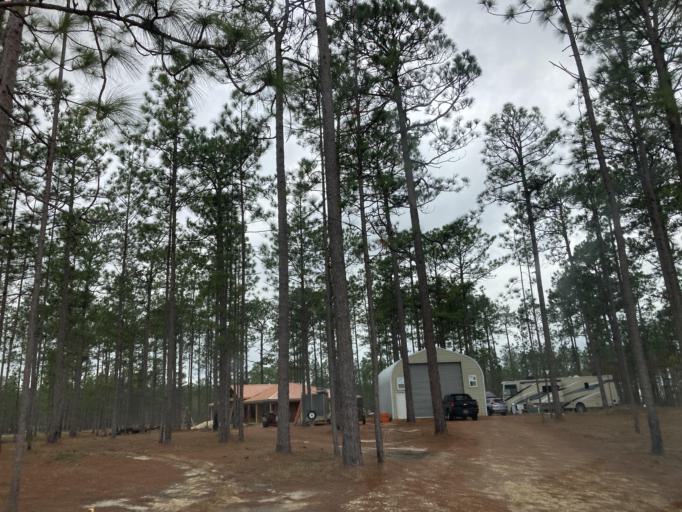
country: US
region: Mississippi
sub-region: Lamar County
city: Lumberton
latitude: 31.0960
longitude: -89.5285
